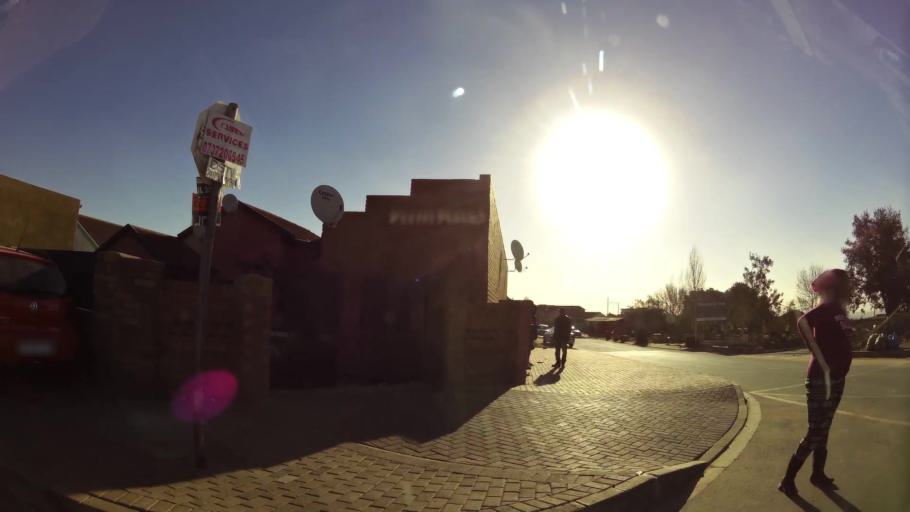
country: ZA
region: Gauteng
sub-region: Ekurhuleni Metropolitan Municipality
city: Tembisa
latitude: -26.0047
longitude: 28.2203
